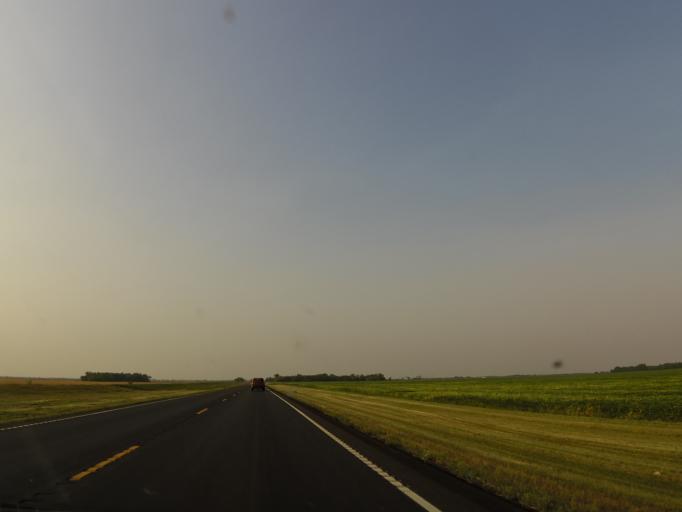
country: US
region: North Dakota
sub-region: Traill County
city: Mayville
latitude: 47.4568
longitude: -97.3260
